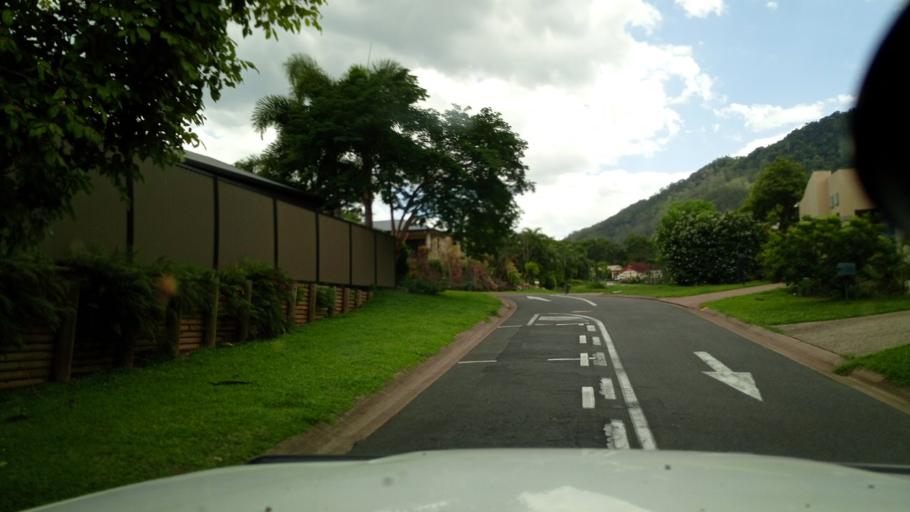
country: AU
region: Queensland
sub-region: Cairns
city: Redlynch
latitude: -16.9099
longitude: 145.7175
